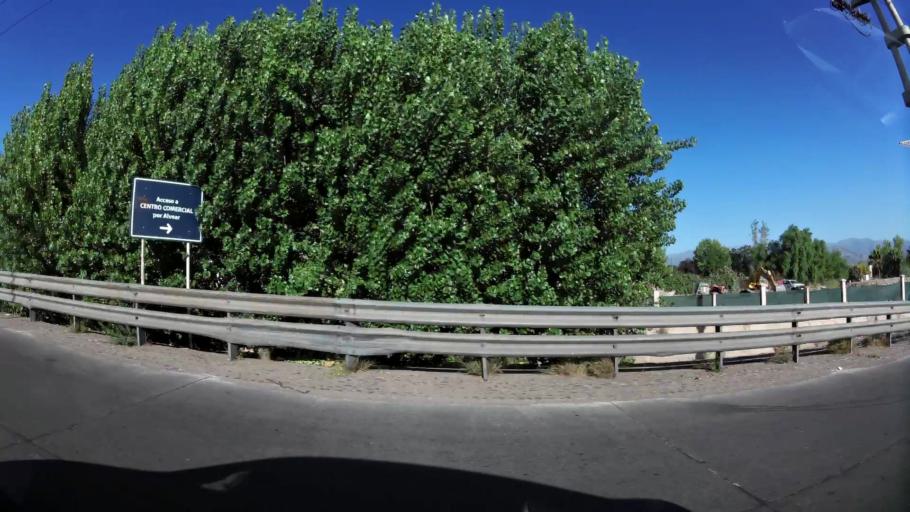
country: AR
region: Mendoza
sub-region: Departamento de Godoy Cruz
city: Godoy Cruz
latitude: -32.9115
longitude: -68.8386
